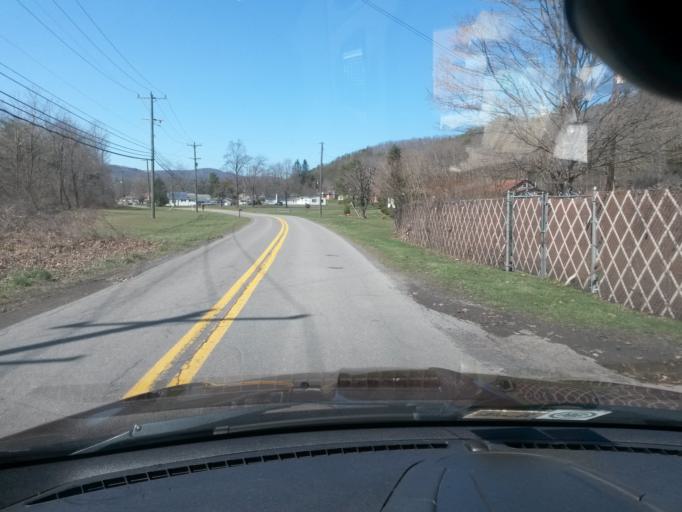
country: US
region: West Virginia
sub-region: Greenbrier County
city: White Sulphur Springs
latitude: 37.7846
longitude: -80.2861
